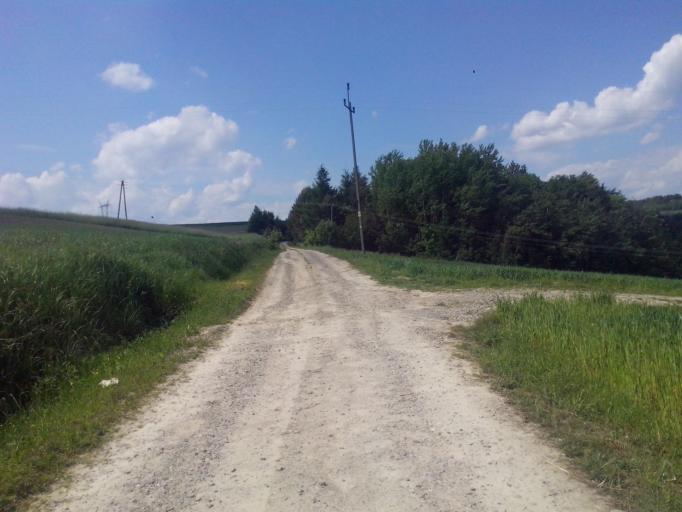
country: PL
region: Subcarpathian Voivodeship
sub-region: Powiat strzyzowski
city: Jawornik
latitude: 49.8383
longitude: 21.8565
